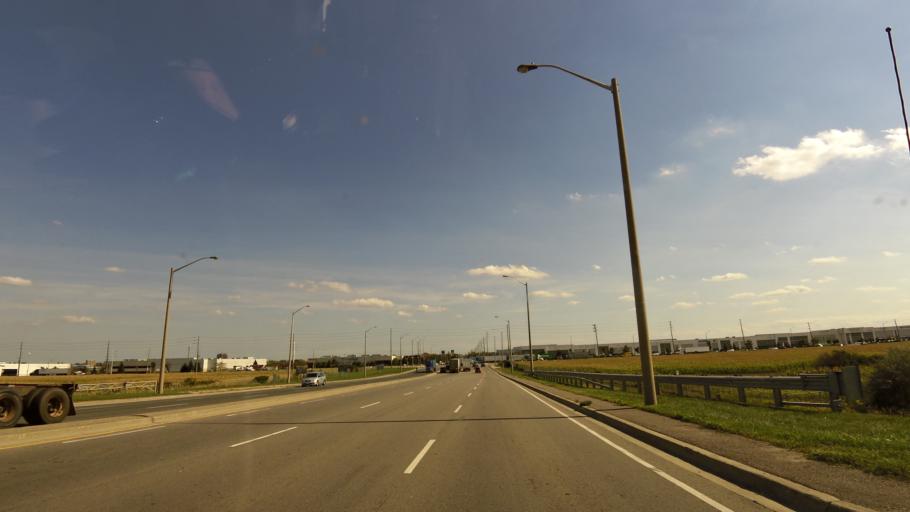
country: CA
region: Ontario
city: Brampton
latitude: 43.7349
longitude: -79.6606
